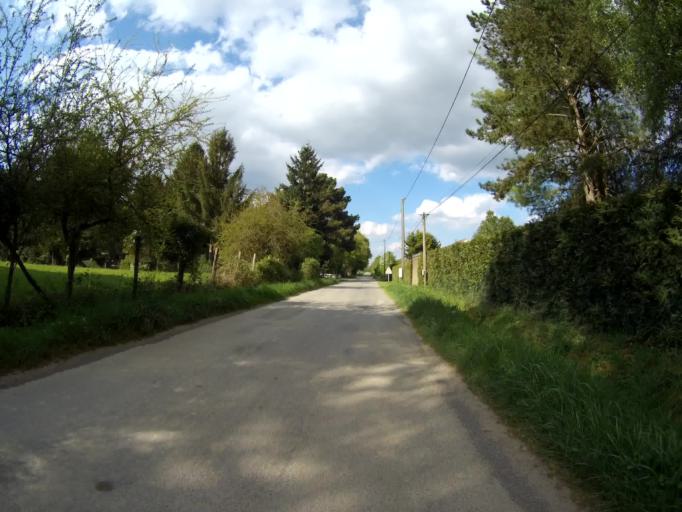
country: FR
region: Brittany
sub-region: Departement d'Ille-et-Vilaine
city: Vern-sur-Seiche
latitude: 48.0552
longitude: -1.5933
